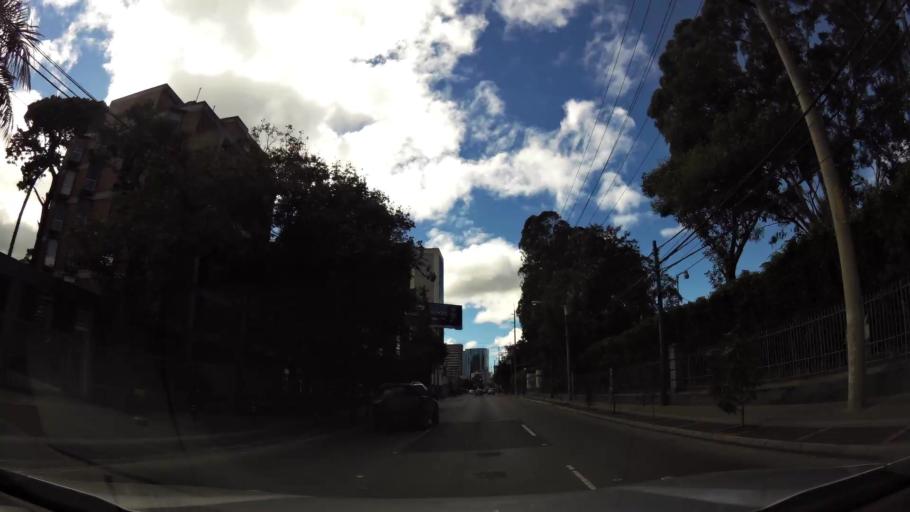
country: GT
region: Guatemala
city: Guatemala City
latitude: 14.6091
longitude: -90.5104
